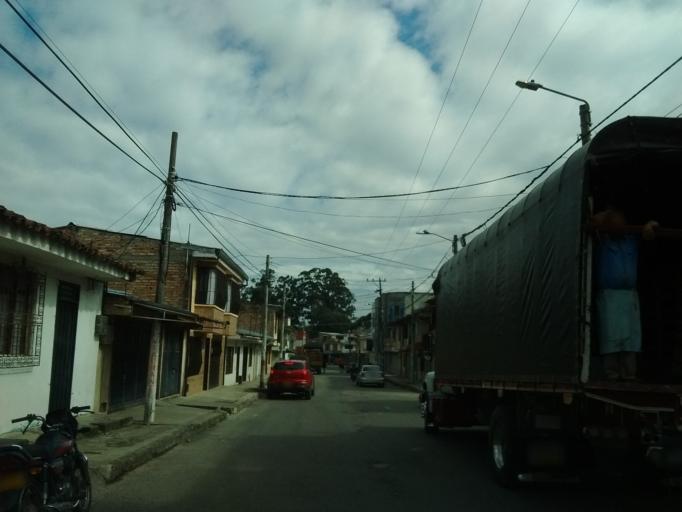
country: CO
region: Cauca
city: Popayan
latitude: 2.4450
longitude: -76.6125
